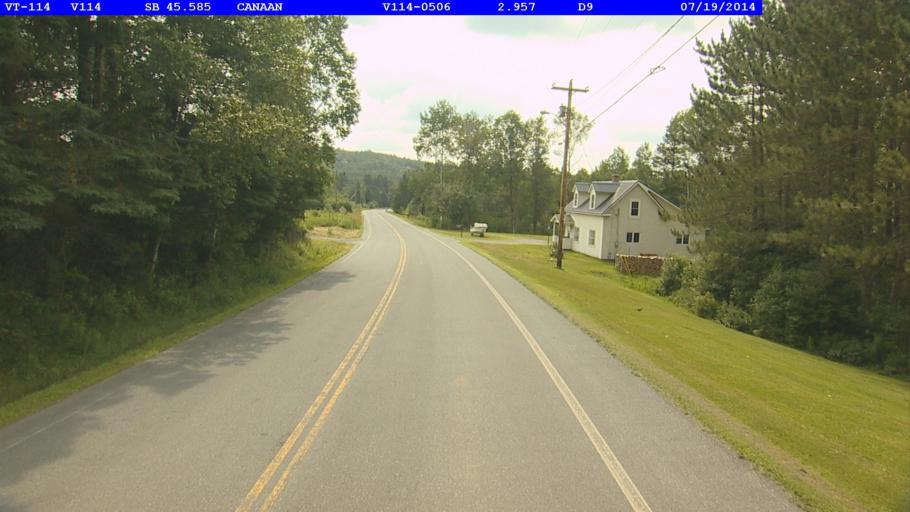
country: US
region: New Hampshire
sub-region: Coos County
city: Colebrook
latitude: 45.0081
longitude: -71.6344
